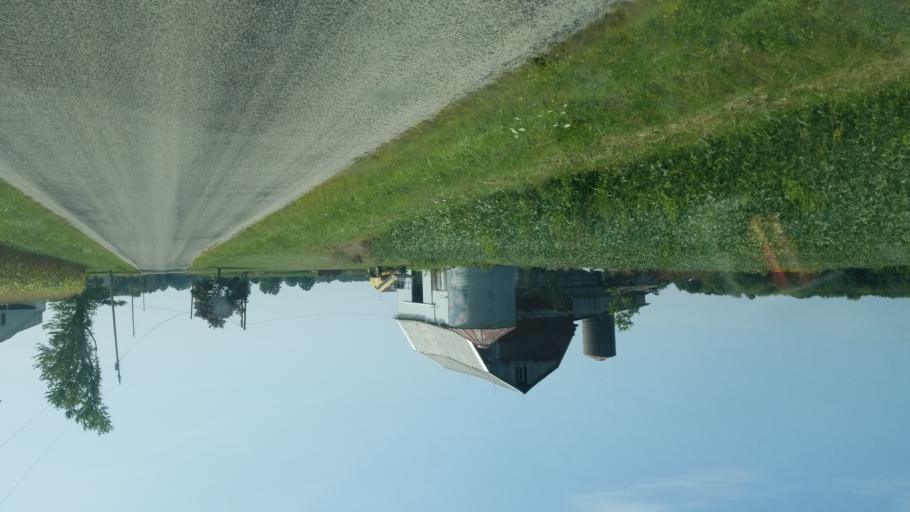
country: US
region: Ohio
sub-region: Crawford County
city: Crestline
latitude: 40.8197
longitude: -82.7063
